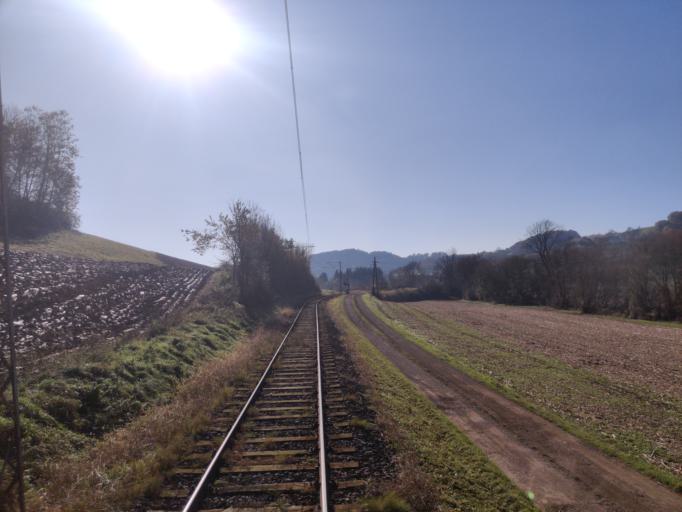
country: AT
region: Styria
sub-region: Politischer Bezirk Suedoststeiermark
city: Maierdorf
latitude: 46.8829
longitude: 15.8535
